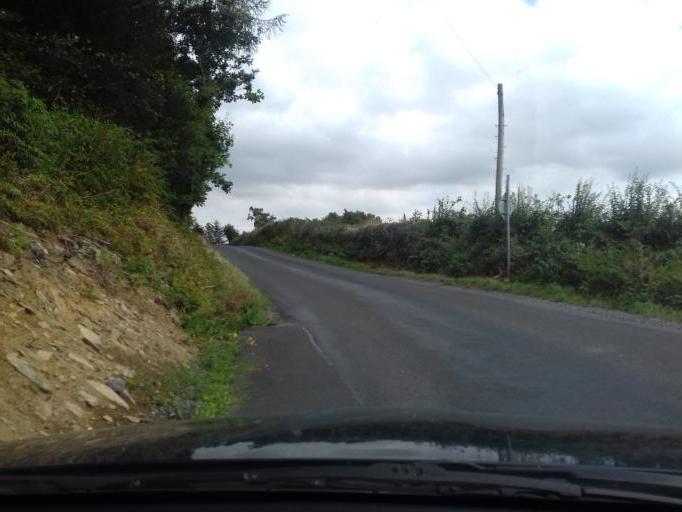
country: IE
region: Leinster
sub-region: Loch Garman
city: Bunclody
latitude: 52.6438
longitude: -6.7200
